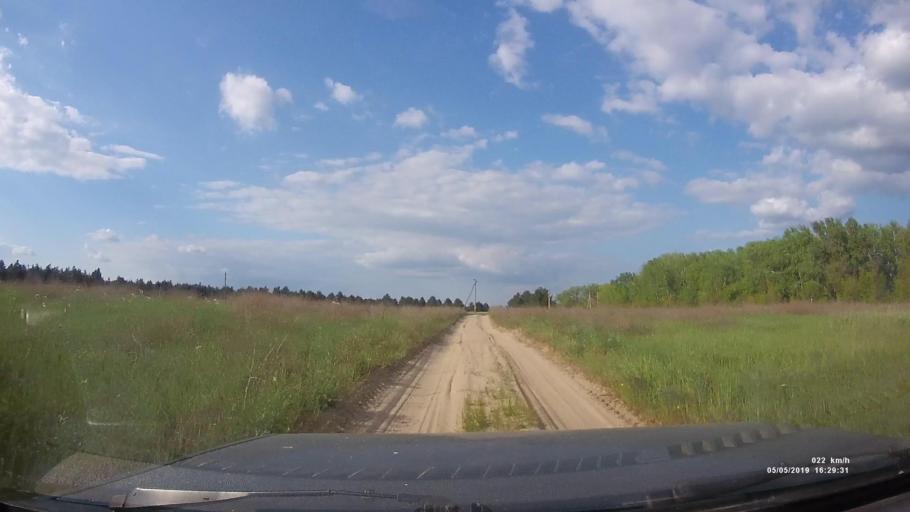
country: RU
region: Rostov
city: Ust'-Donetskiy
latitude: 47.7707
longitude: 41.0143
